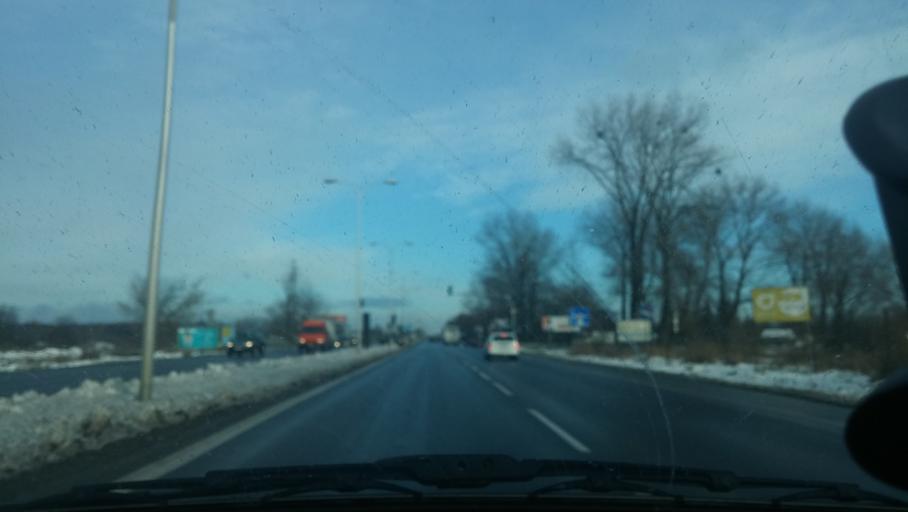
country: PL
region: Masovian Voivodeship
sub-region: Powiat wolominski
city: Zabki
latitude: 52.2933
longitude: 21.0806
